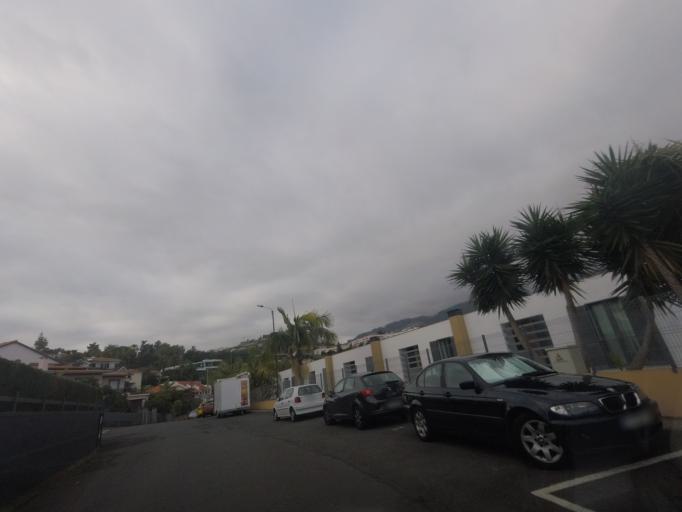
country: PT
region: Madeira
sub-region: Funchal
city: Nossa Senhora do Monte
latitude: 32.6516
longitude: -16.9316
